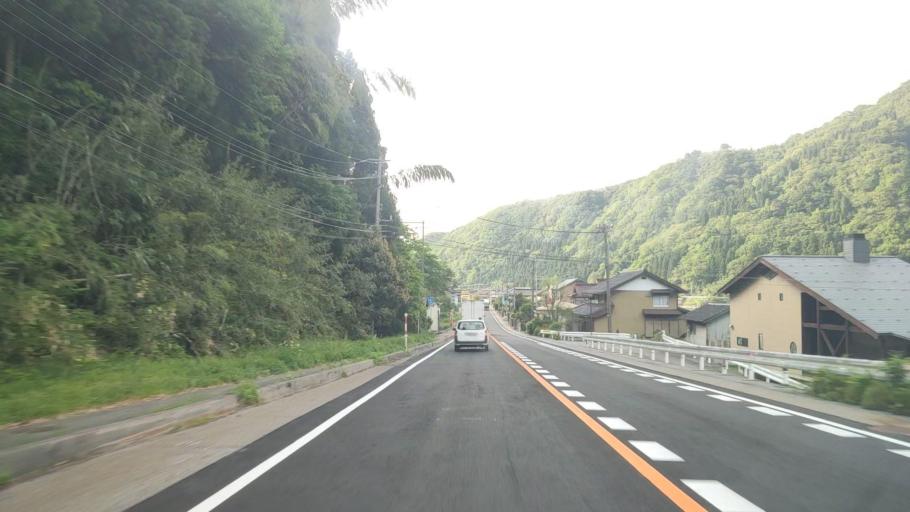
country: JP
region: Toyama
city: Yatsuomachi-higashikumisaka
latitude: 36.5484
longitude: 137.2252
